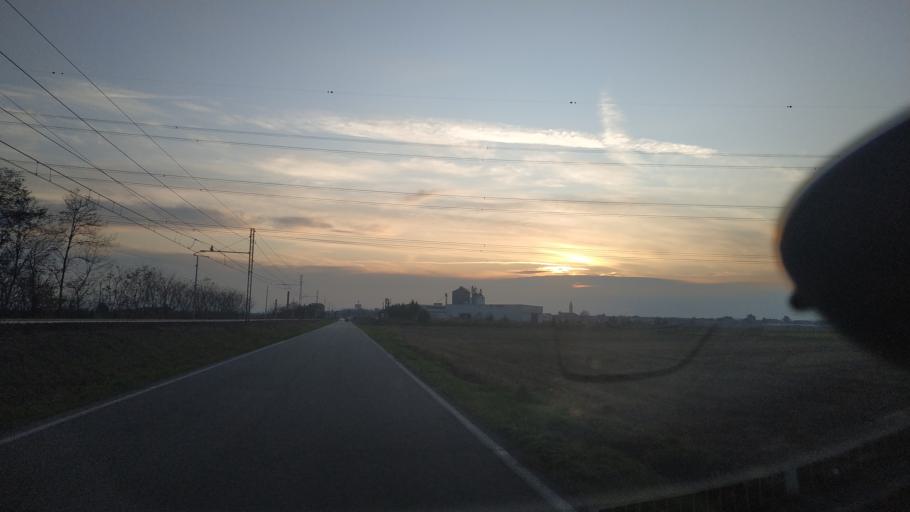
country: IT
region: Piedmont
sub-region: Provincia di Torino
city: Caluso
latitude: 45.2863
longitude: 7.8852
